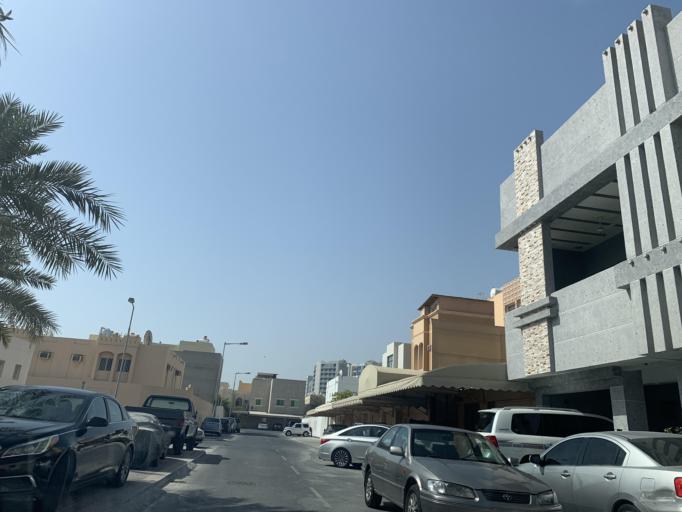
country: BH
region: Muharraq
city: Al Muharraq
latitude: 26.2696
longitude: 50.5982
